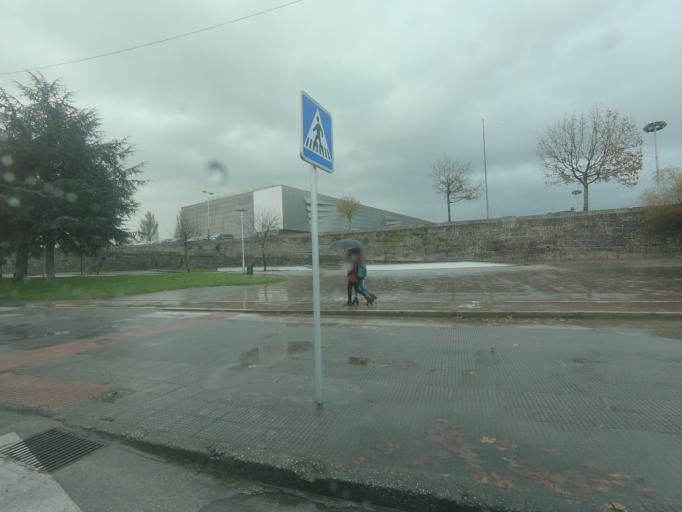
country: ES
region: Galicia
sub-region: Provincia de Pontevedra
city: Pontevedra
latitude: 42.4363
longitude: -8.6410
